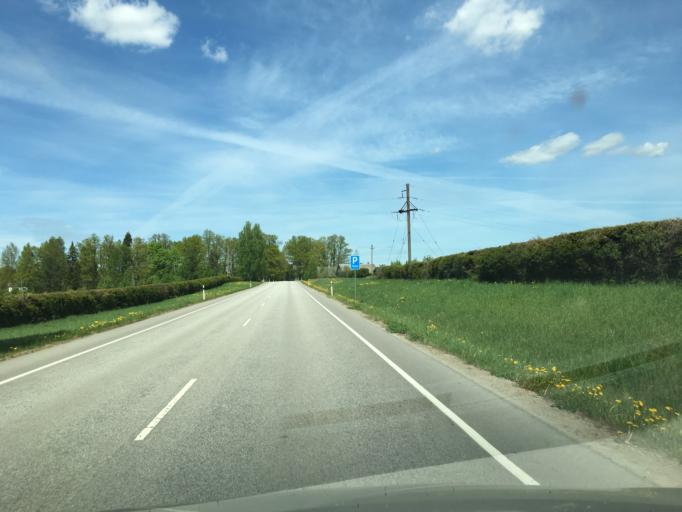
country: EE
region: Vorumaa
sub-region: Antsla vald
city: Vana-Antsla
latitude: 57.8985
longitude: 26.2891
